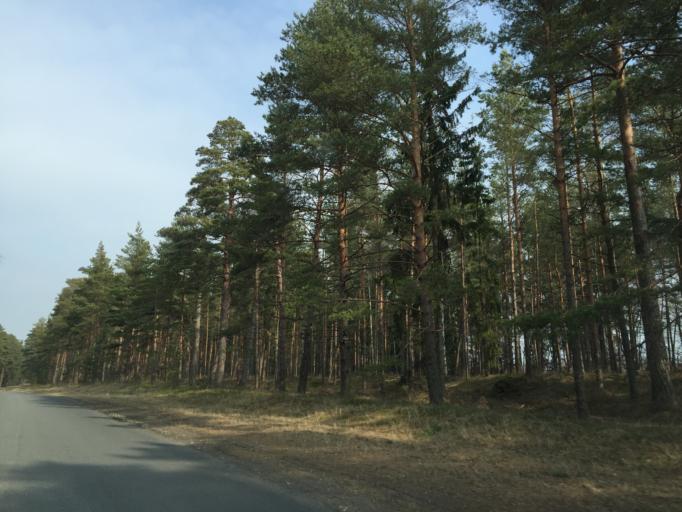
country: LV
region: Salacgrivas
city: Ainazi
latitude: 57.9062
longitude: 24.3800
